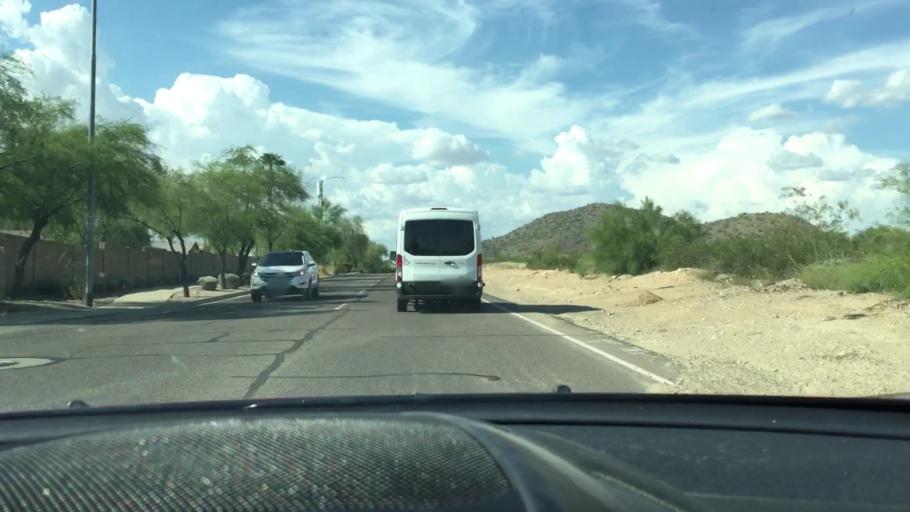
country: US
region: Arizona
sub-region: Maricopa County
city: Paradise Valley
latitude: 33.6643
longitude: -112.0485
